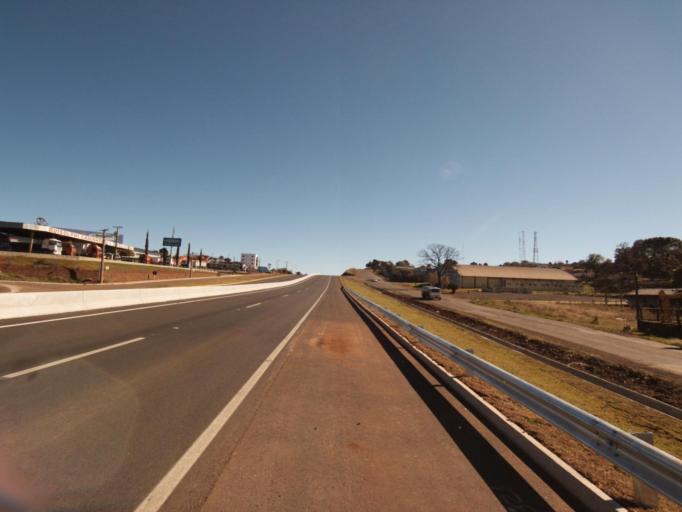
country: BR
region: Santa Catarina
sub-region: Xanxere
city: Xanxere
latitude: -26.8856
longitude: -52.4159
